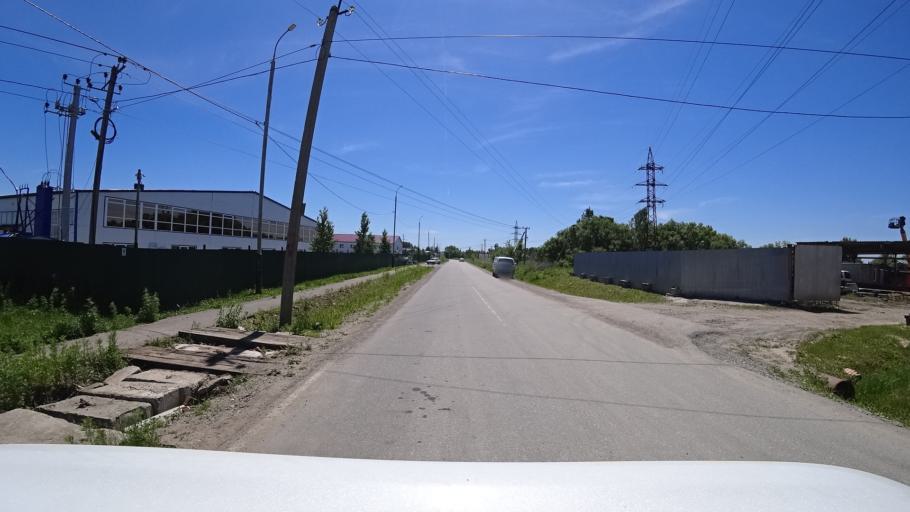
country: RU
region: Khabarovsk Krai
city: Topolevo
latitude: 48.5003
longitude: 135.1838
